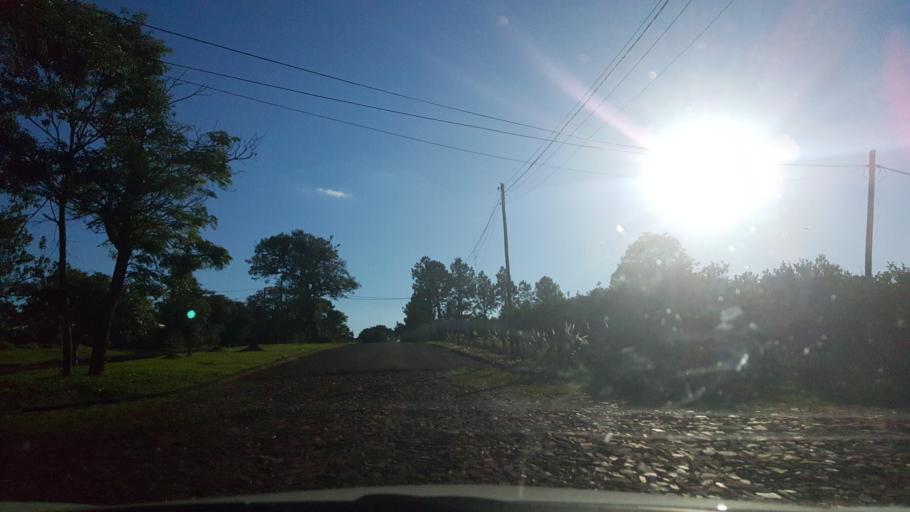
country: AR
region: Misiones
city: Gobernador Roca
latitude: -27.1278
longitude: -55.5019
